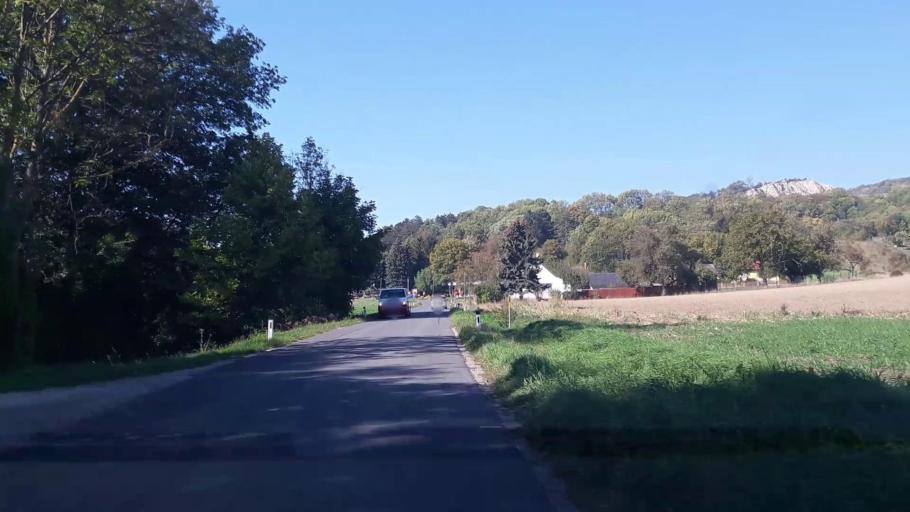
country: AT
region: Lower Austria
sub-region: Politischer Bezirk Korneuburg
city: Ernstbrunn
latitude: 48.5396
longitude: 16.3601
